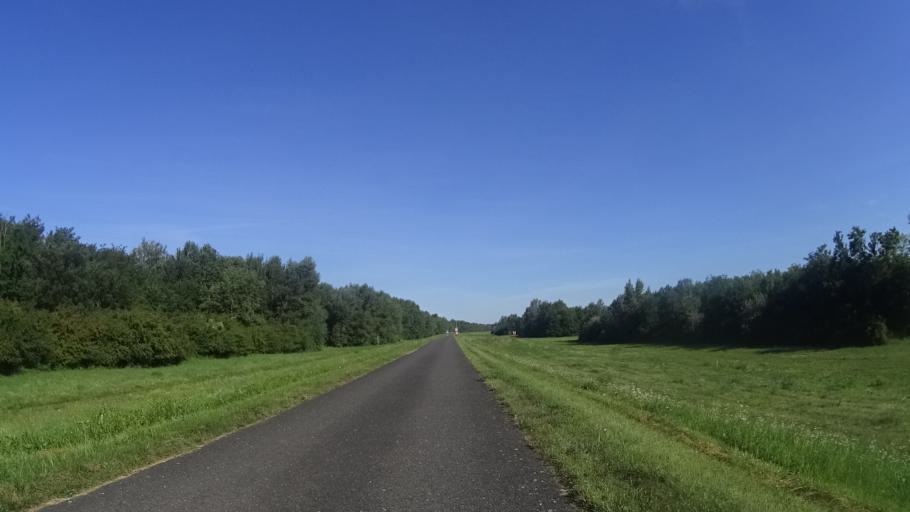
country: HU
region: Gyor-Moson-Sopron
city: Rajka
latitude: 48.0710
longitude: 17.1679
